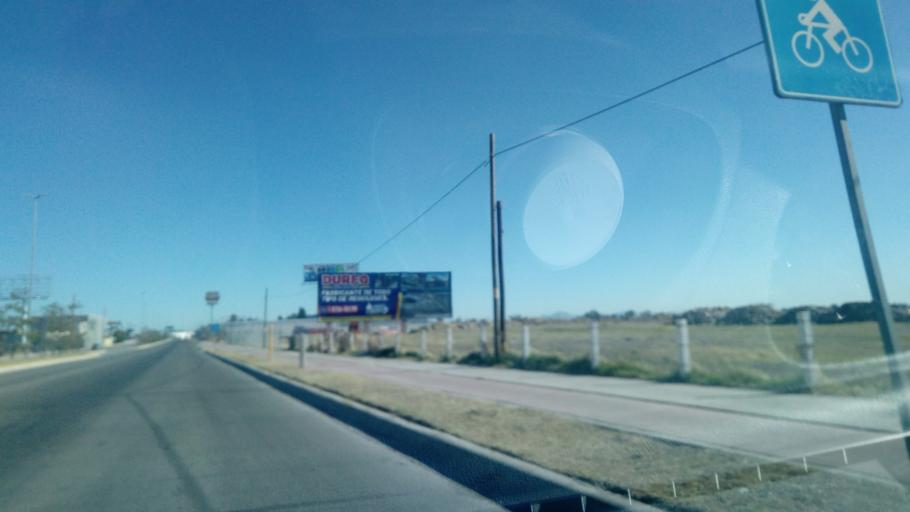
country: MX
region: Durango
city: Victoria de Durango
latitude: 24.0862
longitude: -104.5828
